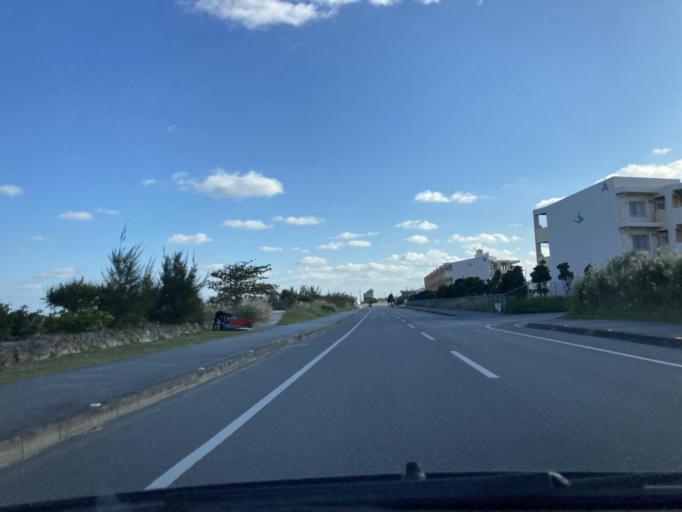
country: JP
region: Okinawa
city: Katsuren-haebaru
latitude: 26.3126
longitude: 127.9193
